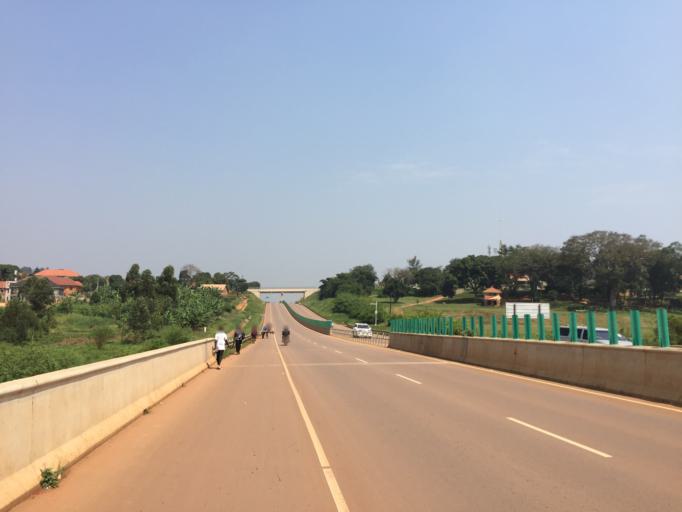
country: UG
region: Central Region
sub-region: Kampala District
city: Kampala
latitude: 0.2376
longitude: 32.6143
